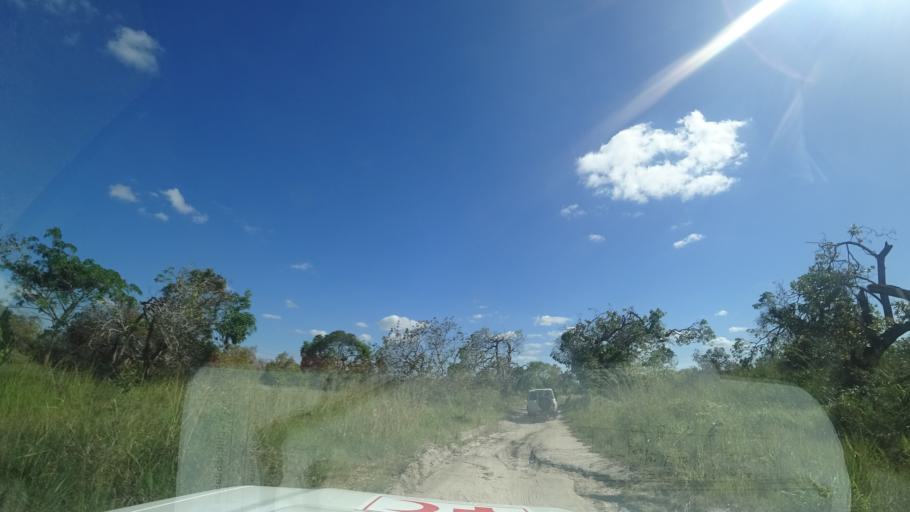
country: MZ
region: Sofala
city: Dondo
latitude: -19.4831
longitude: 34.6199
